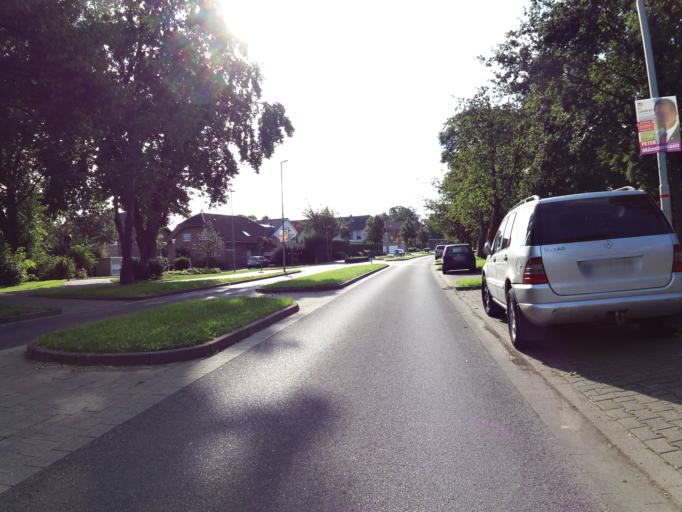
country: DE
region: North Rhine-Westphalia
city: Siersdorf
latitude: 50.8994
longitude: 6.2263
